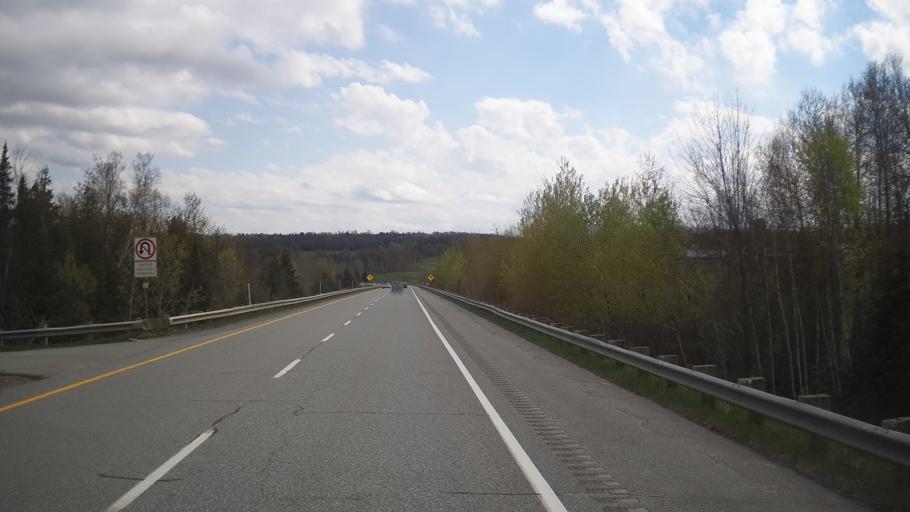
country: CA
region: Quebec
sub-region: Estrie
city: Magog
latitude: 45.1490
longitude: -72.0689
